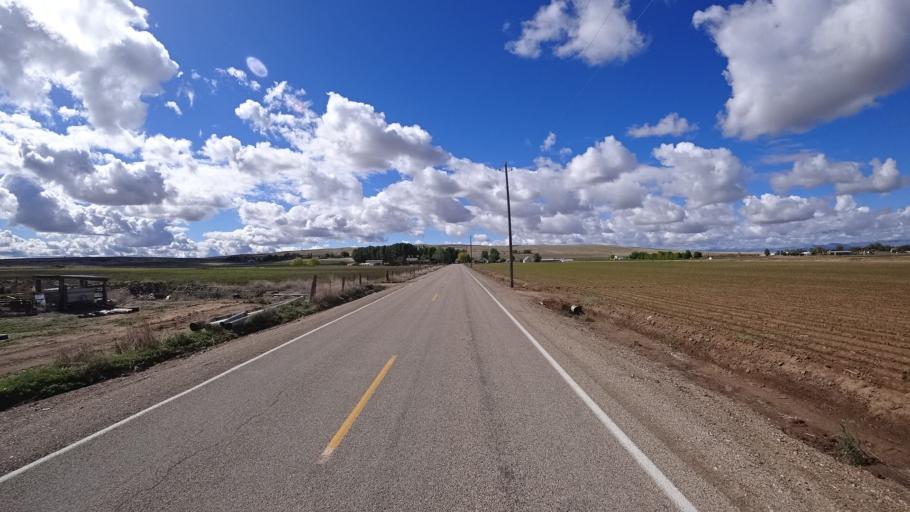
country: US
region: Idaho
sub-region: Ada County
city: Kuna
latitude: 43.4697
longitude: -116.4537
